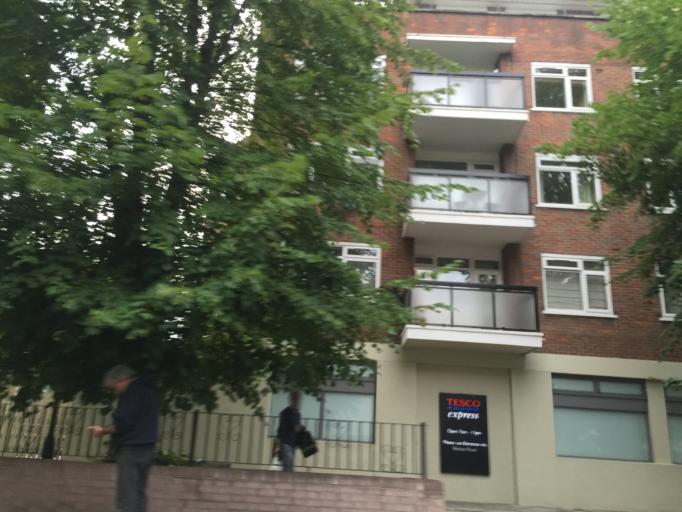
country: GB
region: England
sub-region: Greater London
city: Belsize Park
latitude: 51.5419
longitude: -0.1789
